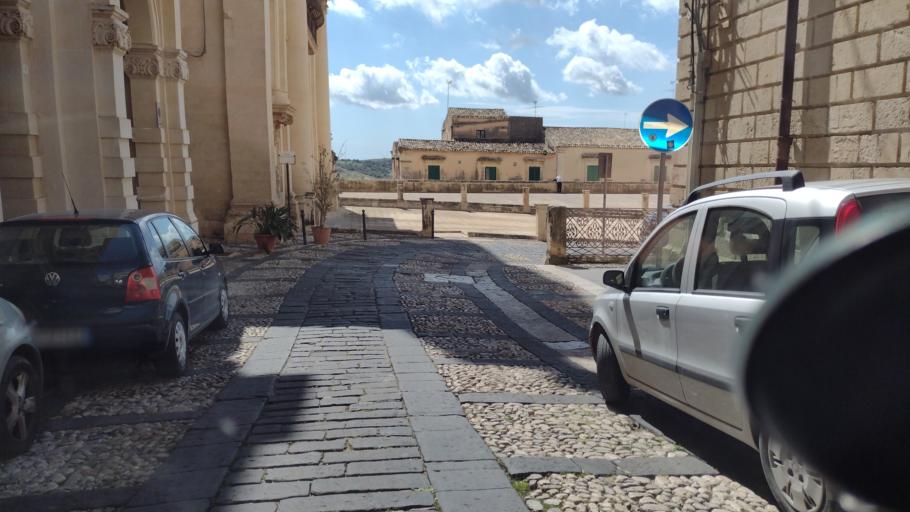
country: IT
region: Sicily
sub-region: Provincia di Siracusa
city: Noto
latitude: 36.8912
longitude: 15.0718
